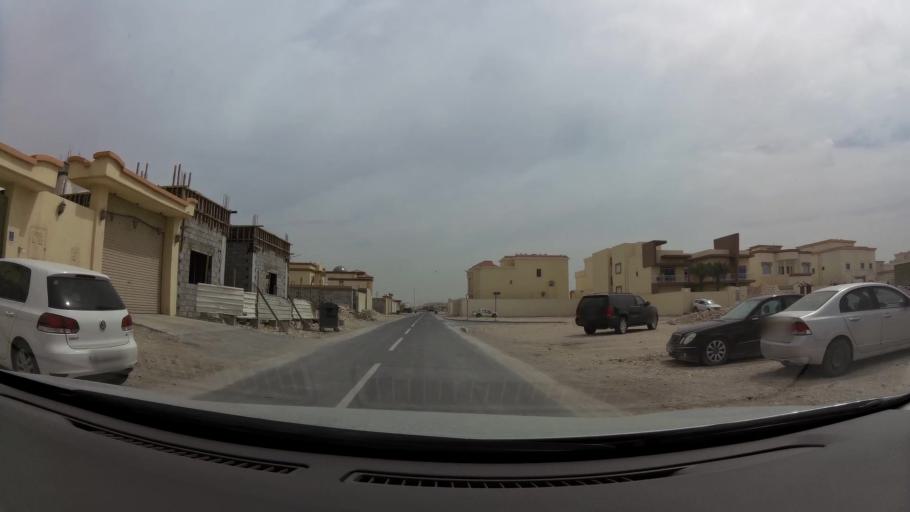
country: QA
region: Baladiyat ad Dawhah
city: Doha
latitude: 25.2160
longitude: 51.4662
